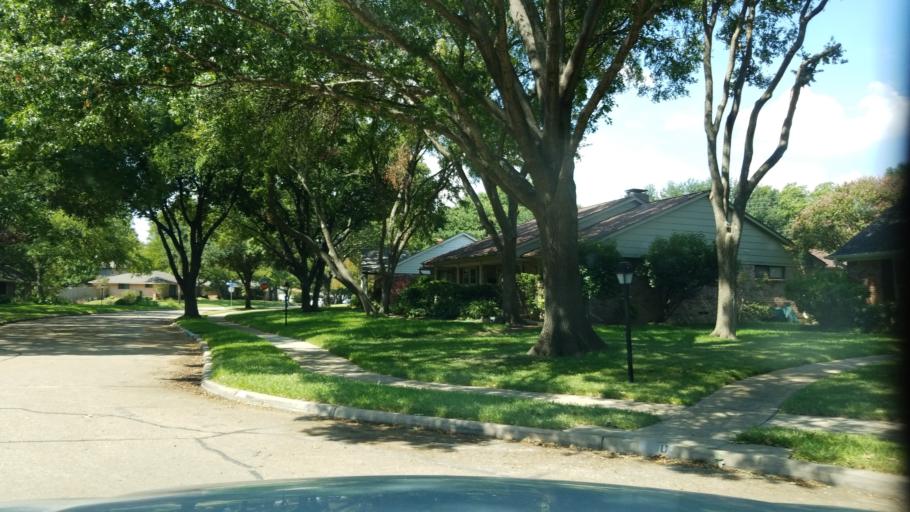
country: US
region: Texas
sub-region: Dallas County
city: Richardson
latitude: 32.9604
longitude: -96.7521
